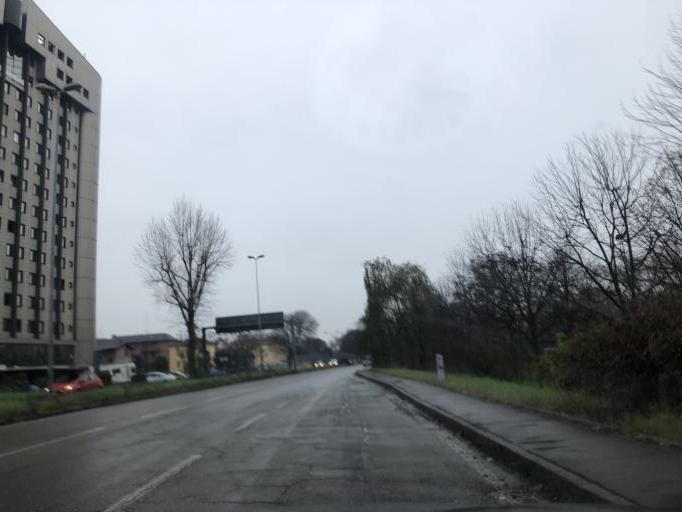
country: IT
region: Emilia-Romagna
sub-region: Provincia di Modena
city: Modena
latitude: 44.6356
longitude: 10.8973
